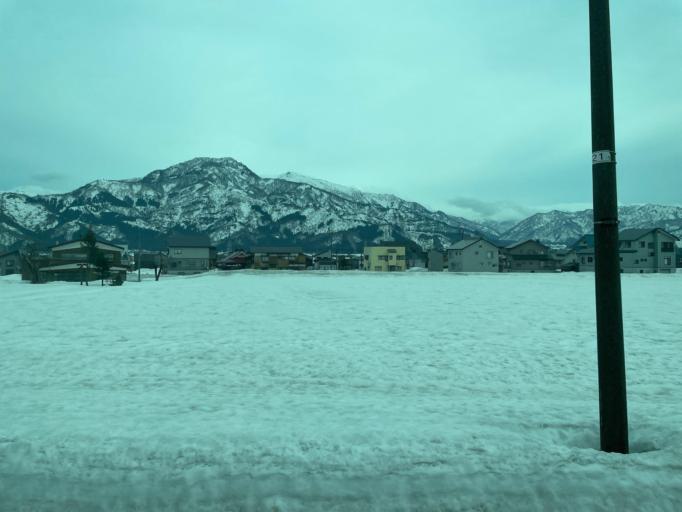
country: JP
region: Niigata
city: Shiozawa
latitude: 37.0499
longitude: 138.8624
